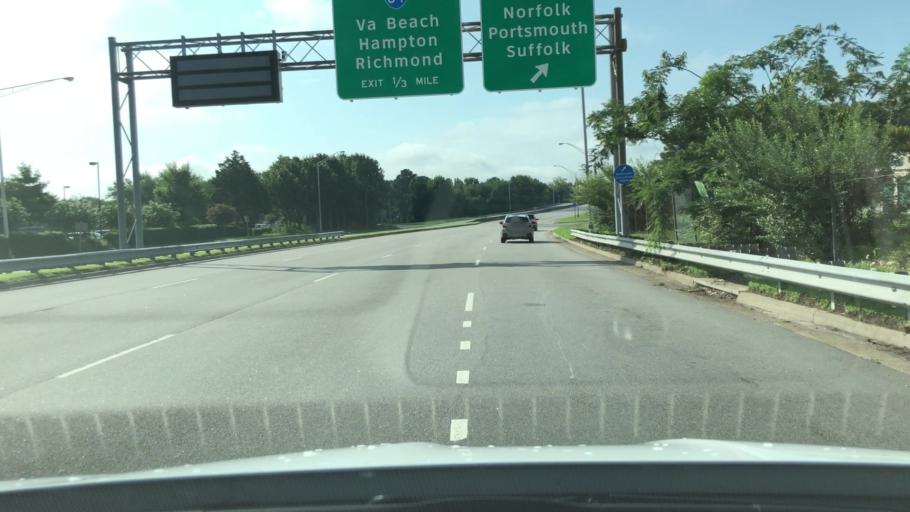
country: US
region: Virginia
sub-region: City of Chesapeake
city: Chesapeake
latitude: 36.7886
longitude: -76.2362
